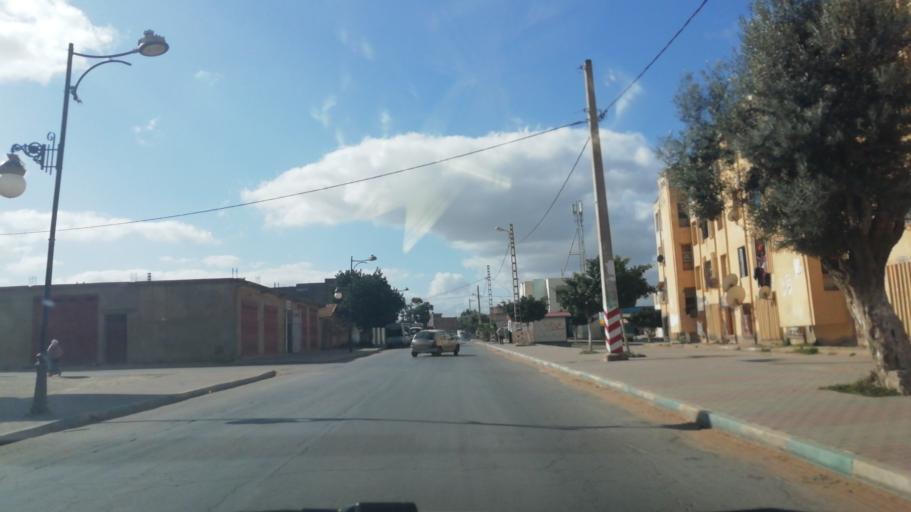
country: DZ
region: Relizane
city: Mazouna
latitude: 36.2727
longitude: 0.6336
